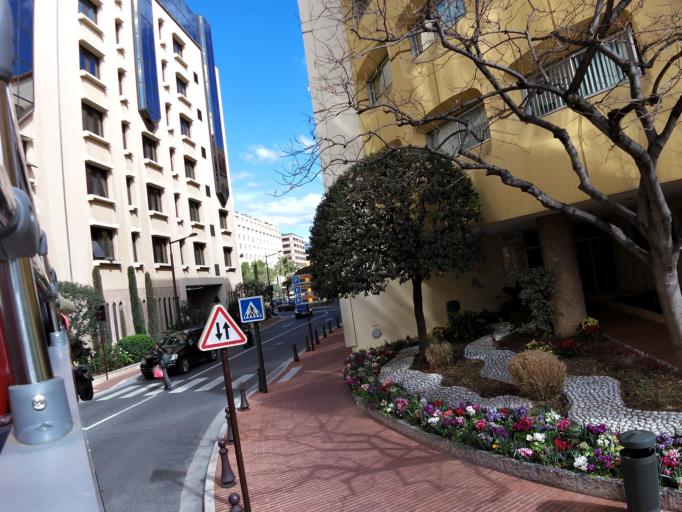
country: MC
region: Commune de Monaco
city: Fontvieille
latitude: 43.7273
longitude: 7.4140
